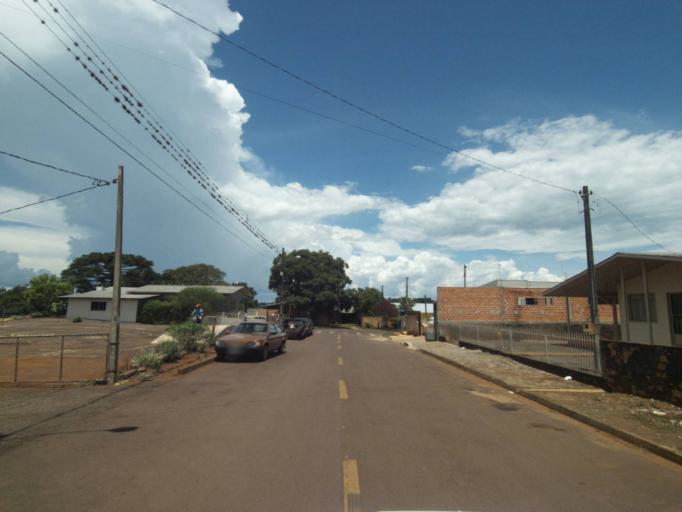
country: BR
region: Parana
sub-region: Guaraniacu
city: Guaraniacu
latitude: -25.1001
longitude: -52.8629
